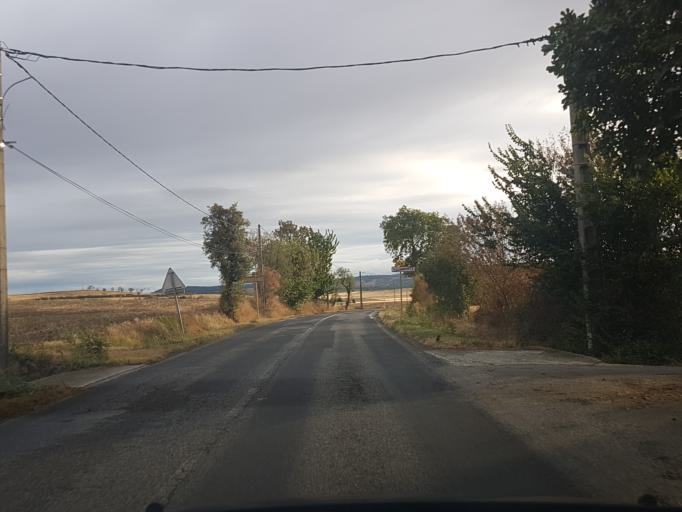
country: FR
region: Languedoc-Roussillon
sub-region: Departement de l'Aude
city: Bram
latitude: 43.2272
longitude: 2.0922
